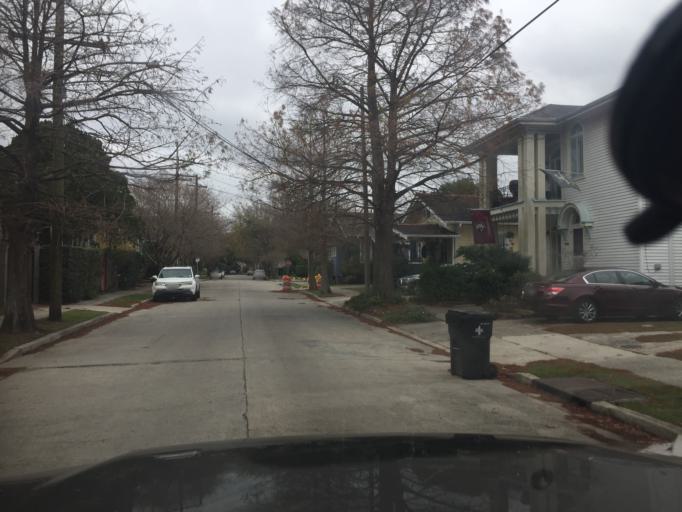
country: US
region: Louisiana
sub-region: Orleans Parish
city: New Orleans
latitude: 29.9779
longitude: -90.0841
